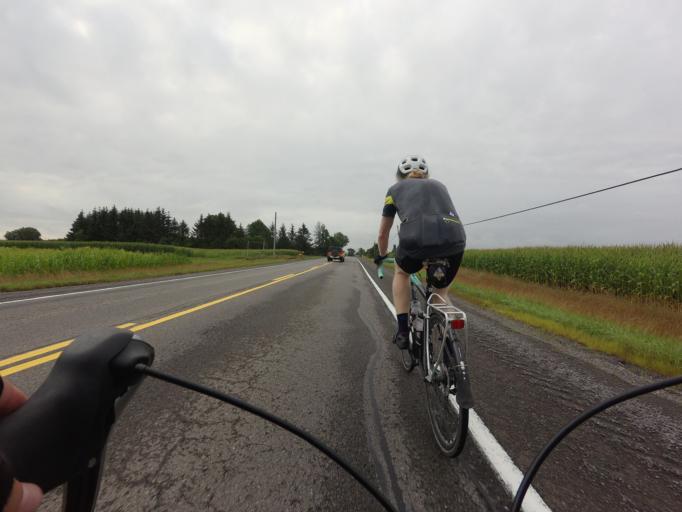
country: CA
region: Ontario
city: Bells Corners
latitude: 45.1836
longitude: -75.8110
